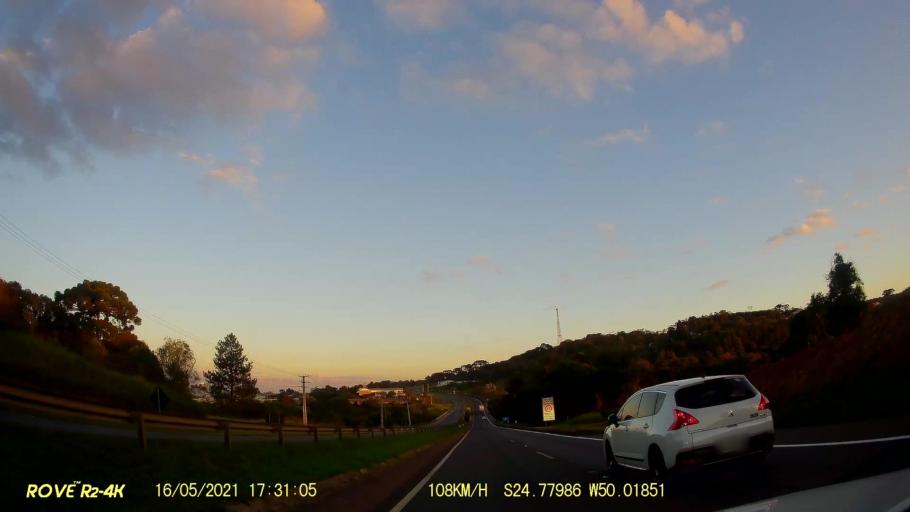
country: BR
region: Parana
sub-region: Castro
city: Castro
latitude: -24.7802
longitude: -50.0184
